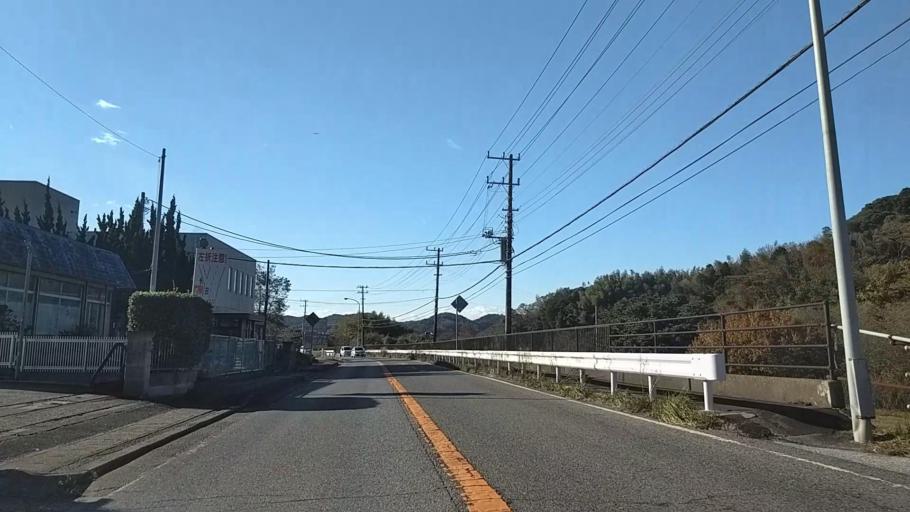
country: JP
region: Chiba
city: Futtsu
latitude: 35.2289
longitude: 139.8746
